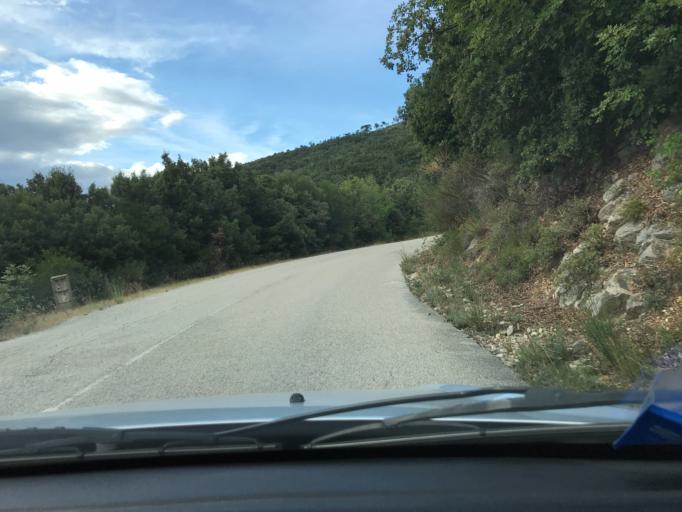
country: IT
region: Umbria
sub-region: Provincia di Terni
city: Montecchio
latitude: 42.6856
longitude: 12.2975
